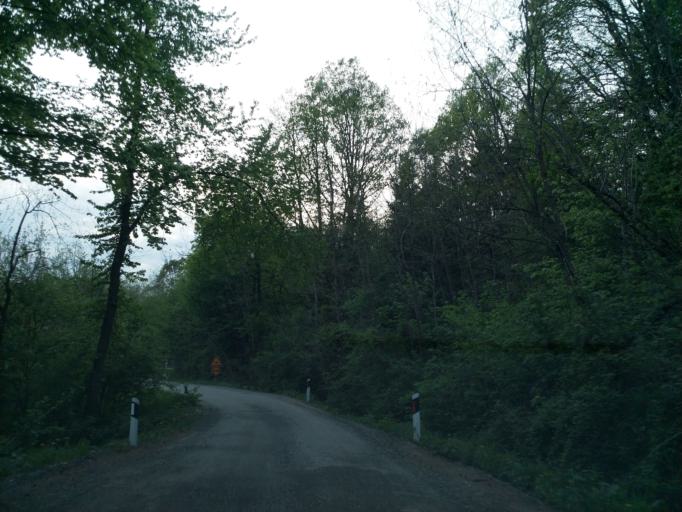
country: RS
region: Central Serbia
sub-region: Pomoravski Okrug
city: Despotovac
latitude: 43.9623
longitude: 21.5625
